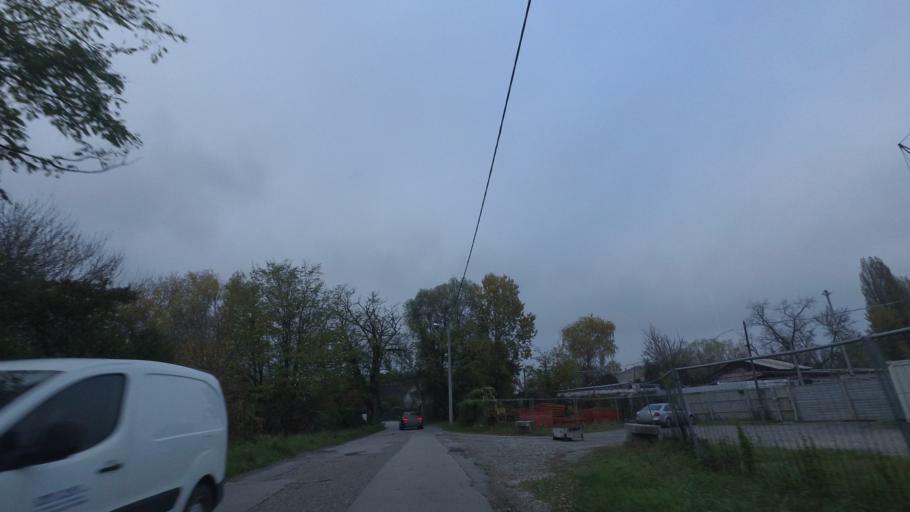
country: HR
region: Grad Zagreb
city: Novi Zagreb
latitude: 45.7888
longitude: 16.0275
